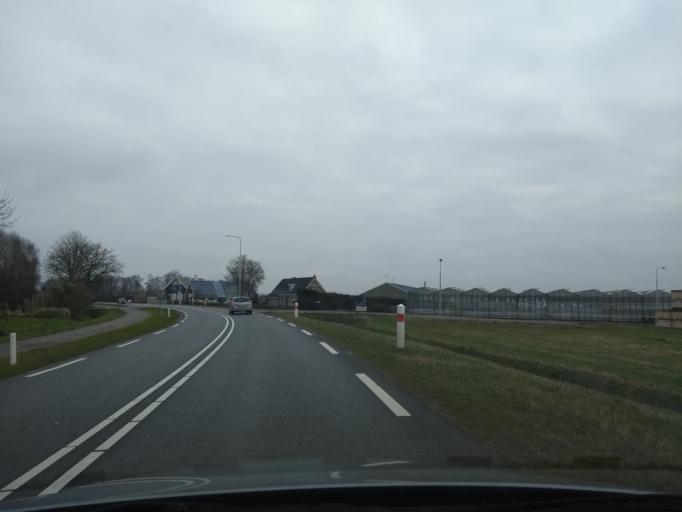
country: NL
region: Flevoland
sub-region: Gemeente Noordoostpolder
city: Ens
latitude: 52.7139
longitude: 5.8685
